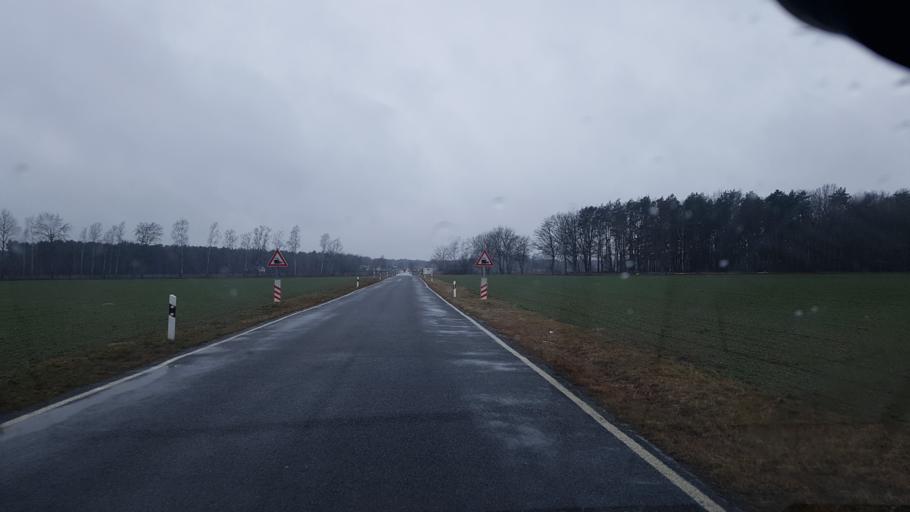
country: DE
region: Brandenburg
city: Cottbus
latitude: 51.6980
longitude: 14.4030
